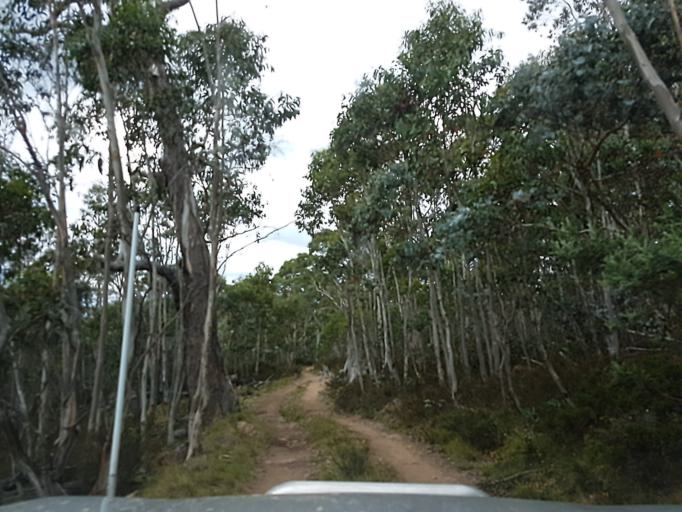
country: AU
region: New South Wales
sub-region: Snowy River
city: Jindabyne
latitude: -36.8818
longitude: 148.1507
